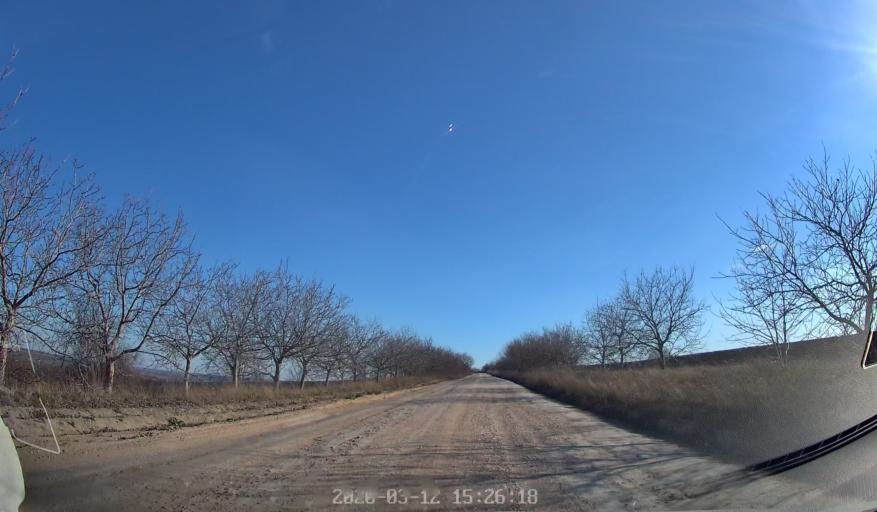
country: MD
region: Chisinau
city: Ciorescu
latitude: 47.1789
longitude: 28.9229
